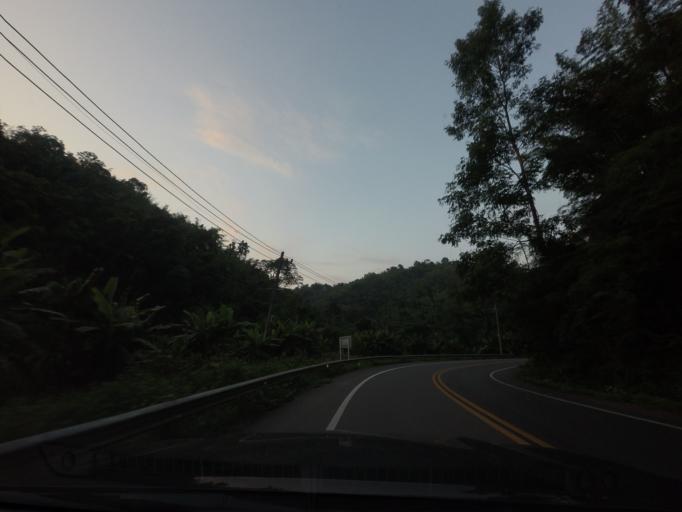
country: TH
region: Nan
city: Na Noi
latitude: 18.4277
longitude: 100.6947
